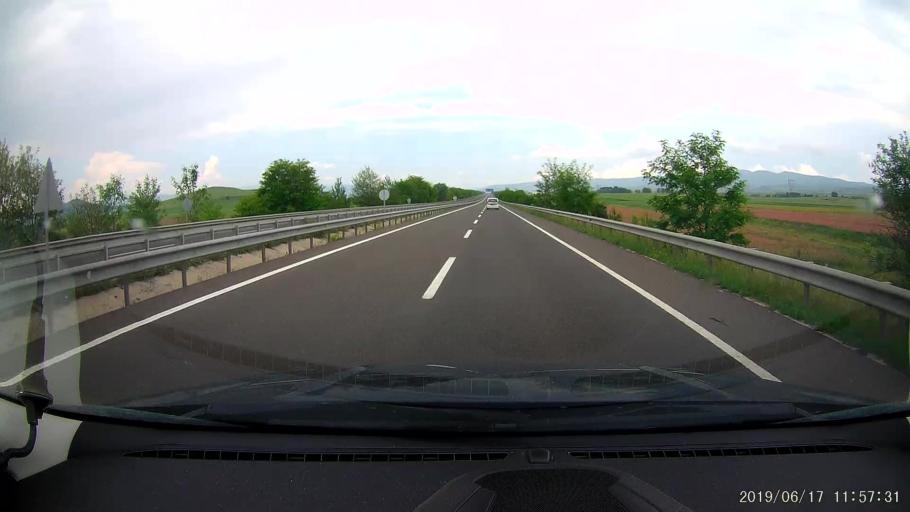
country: TR
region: Cankiri
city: Cerkes
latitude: 40.8078
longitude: 32.9562
